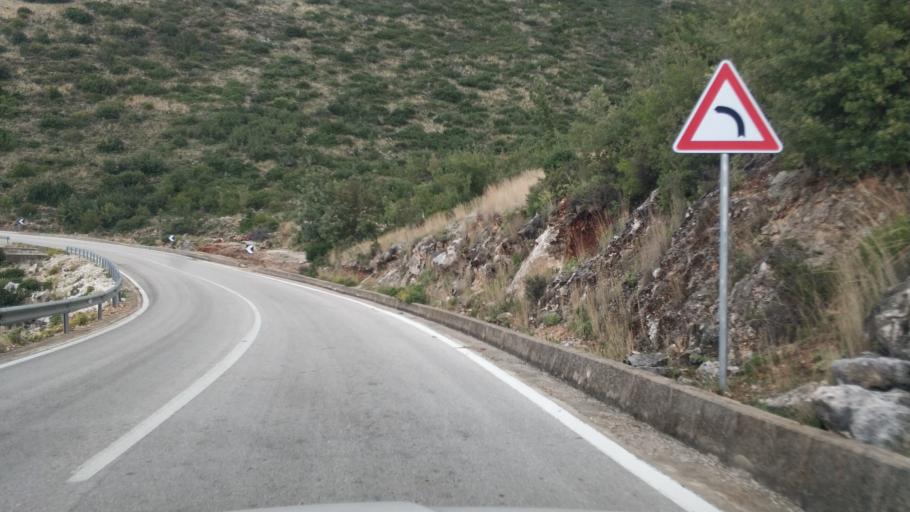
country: AL
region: Vlore
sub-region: Rrethi i Vlores
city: Vranisht
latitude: 40.1452
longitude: 19.6605
